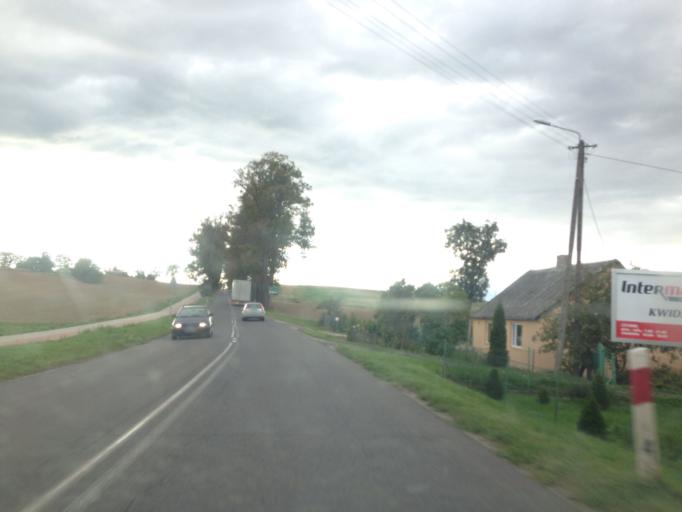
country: PL
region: Pomeranian Voivodeship
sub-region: Powiat kwidzynski
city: Kwidzyn
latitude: 53.7266
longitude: 19.0142
